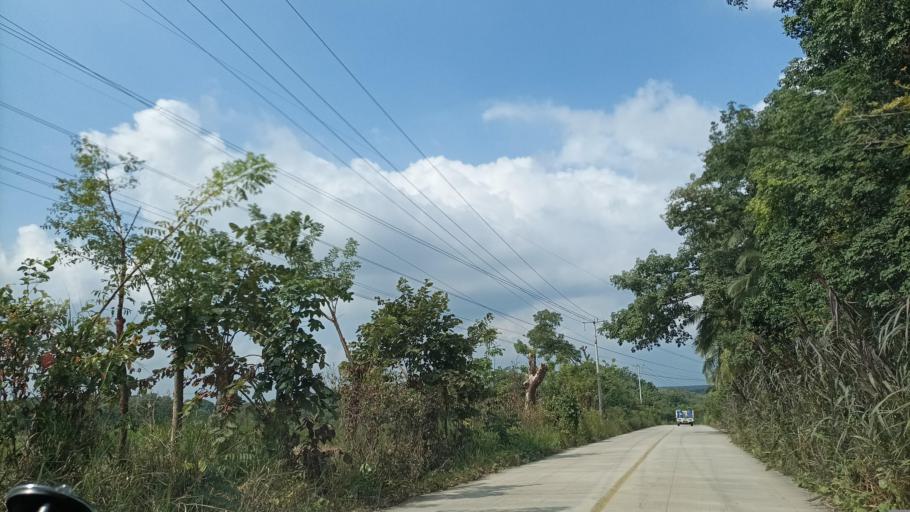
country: MX
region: Veracruz
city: Las Choapas
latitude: 17.7928
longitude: -94.1102
